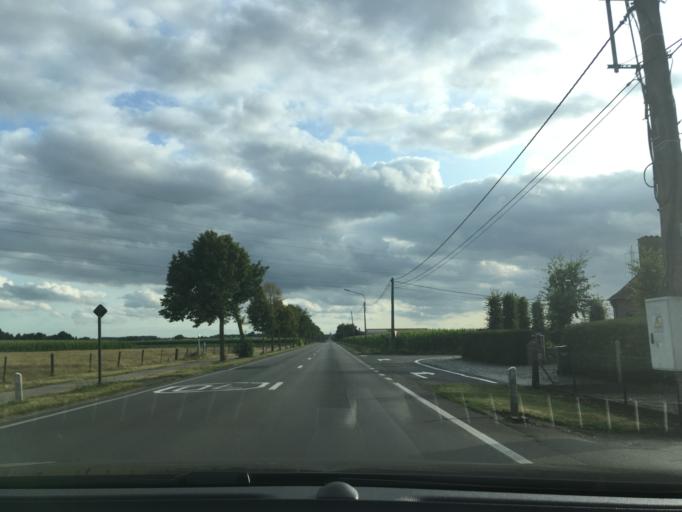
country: BE
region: Flanders
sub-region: Provincie West-Vlaanderen
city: Staden
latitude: 50.9578
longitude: 3.0515
